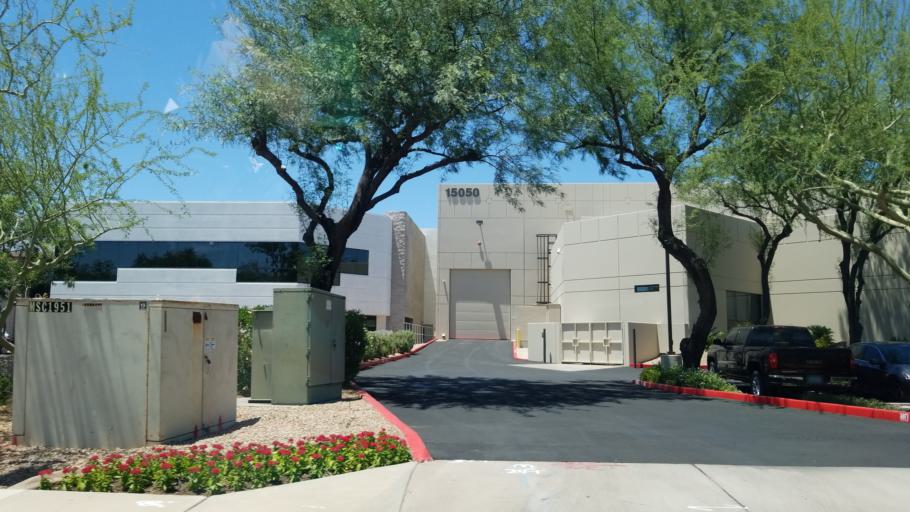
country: US
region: Arizona
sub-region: Maricopa County
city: Paradise Valley
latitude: 33.6221
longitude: -111.9075
